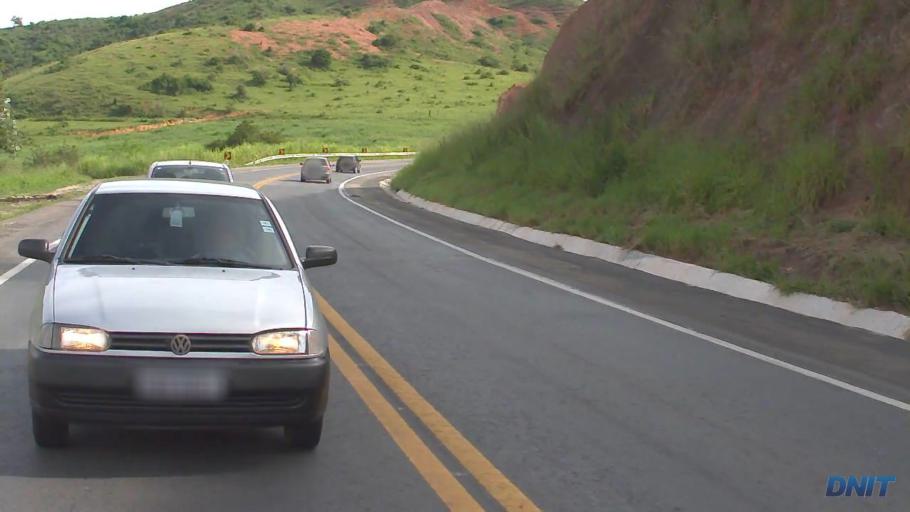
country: BR
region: Minas Gerais
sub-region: Belo Oriente
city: Belo Oriente
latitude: -19.2222
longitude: -42.3143
